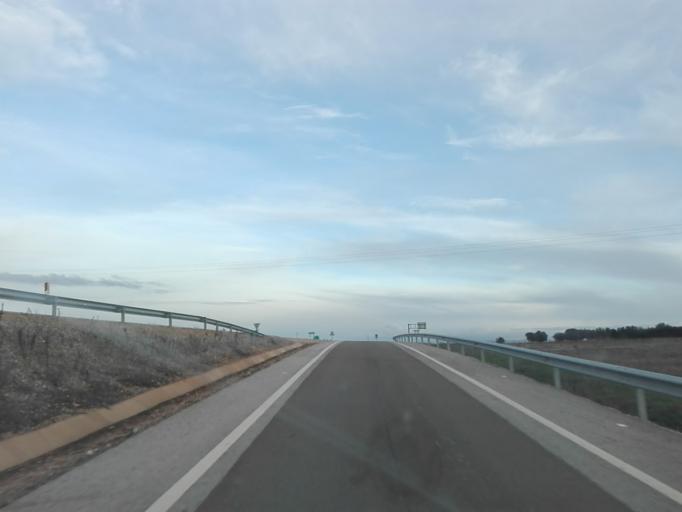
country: ES
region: Extremadura
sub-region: Provincia de Badajoz
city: Usagre
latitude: 38.3445
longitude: -6.1706
